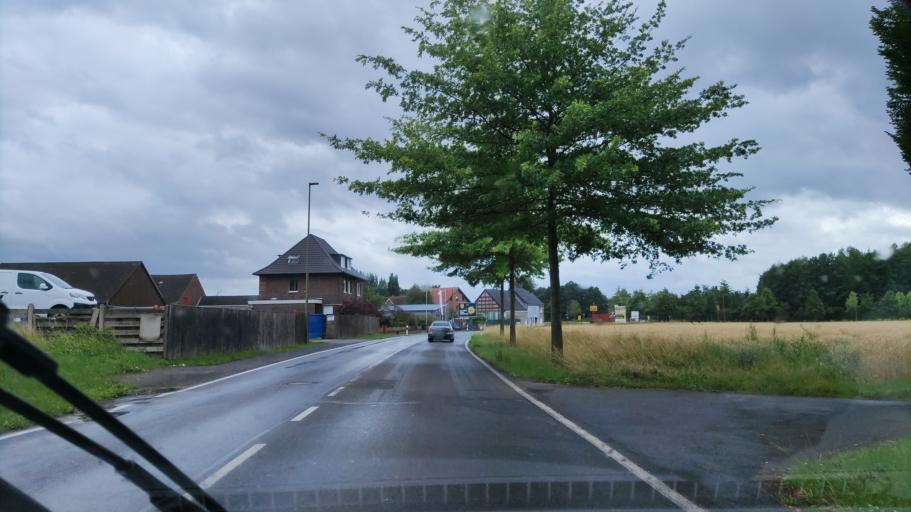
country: DE
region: North Rhine-Westphalia
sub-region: Regierungsbezirk Arnsberg
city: Hamm
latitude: 51.7118
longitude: 7.8361
